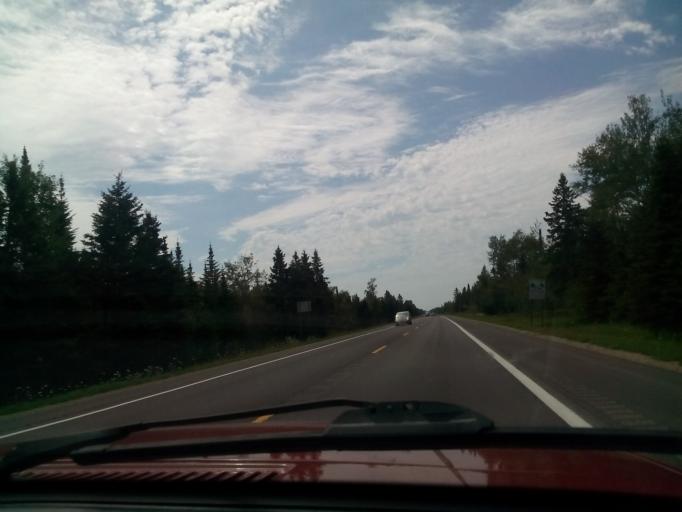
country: US
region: Michigan
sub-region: Schoolcraft County
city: Manistique
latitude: 46.0450
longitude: -85.9698
